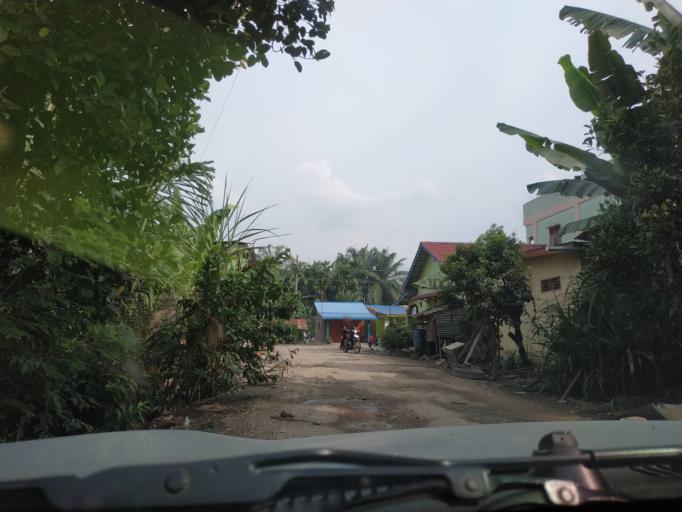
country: ID
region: North Sumatra
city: Rantauprapat
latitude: 2.1867
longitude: 100.0317
